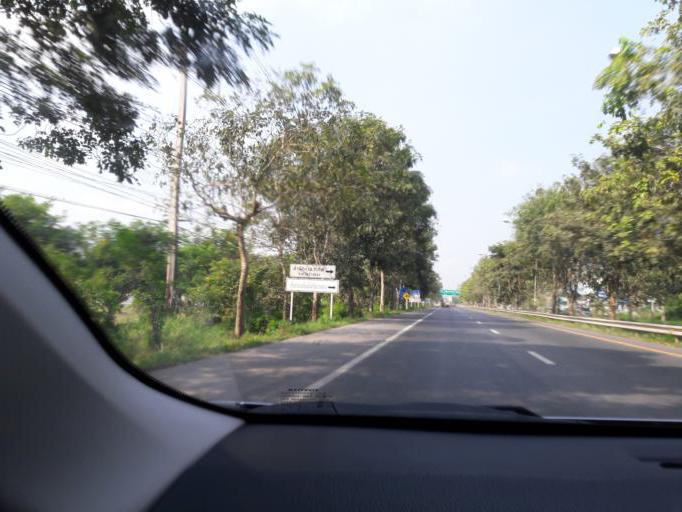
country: TH
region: Ang Thong
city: Ang Thong
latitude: 14.5773
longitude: 100.4582
